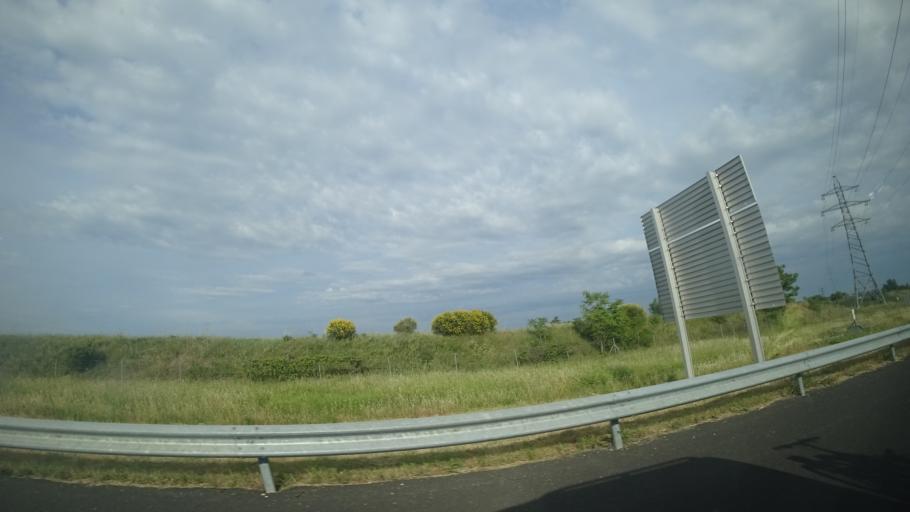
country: FR
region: Languedoc-Roussillon
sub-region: Departement de l'Herault
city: Nebian
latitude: 43.6017
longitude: 3.4613
